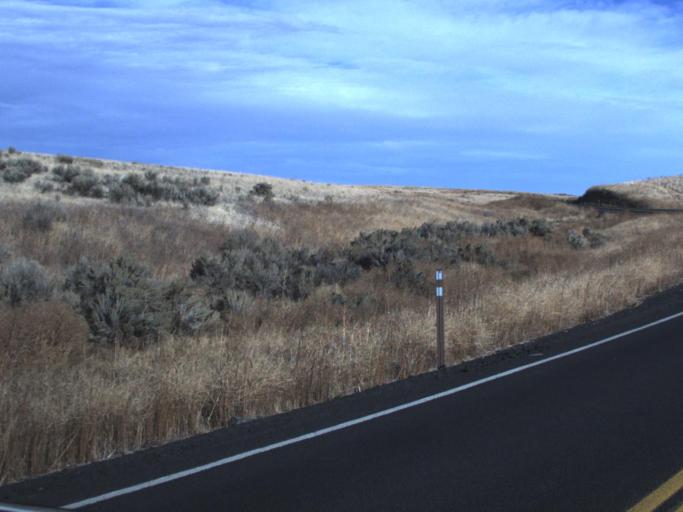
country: US
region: Washington
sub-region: Adams County
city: Ritzville
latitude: 47.1801
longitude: -118.6880
